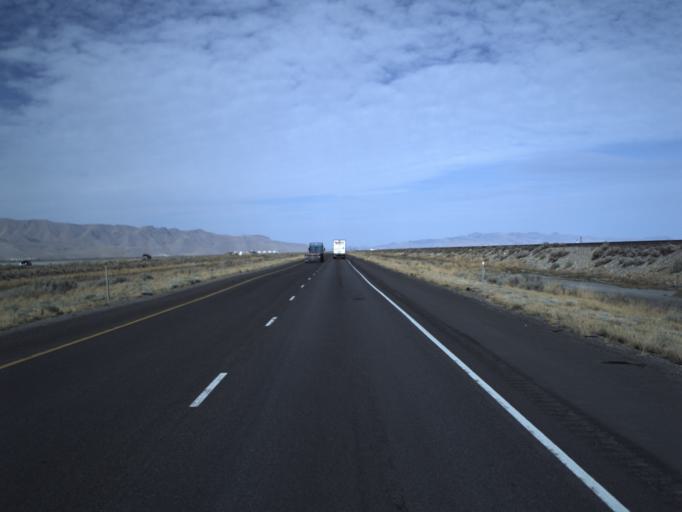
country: US
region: Utah
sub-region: Tooele County
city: Grantsville
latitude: 40.6769
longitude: -112.4052
